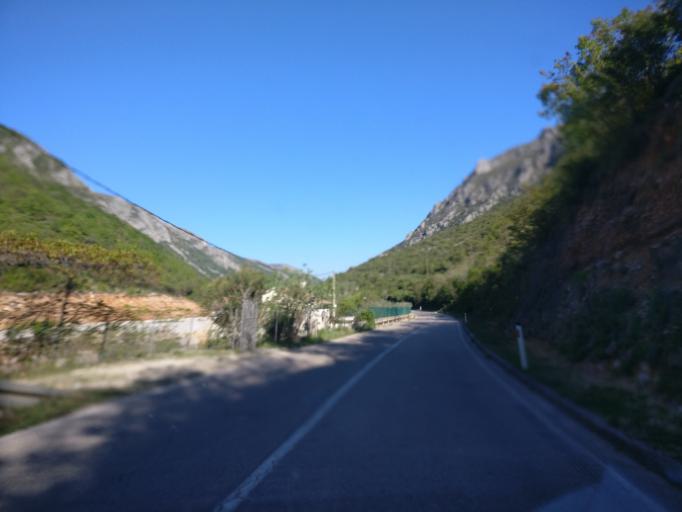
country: BA
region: Federation of Bosnia and Herzegovina
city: Stolac
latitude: 43.0747
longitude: 18.0294
